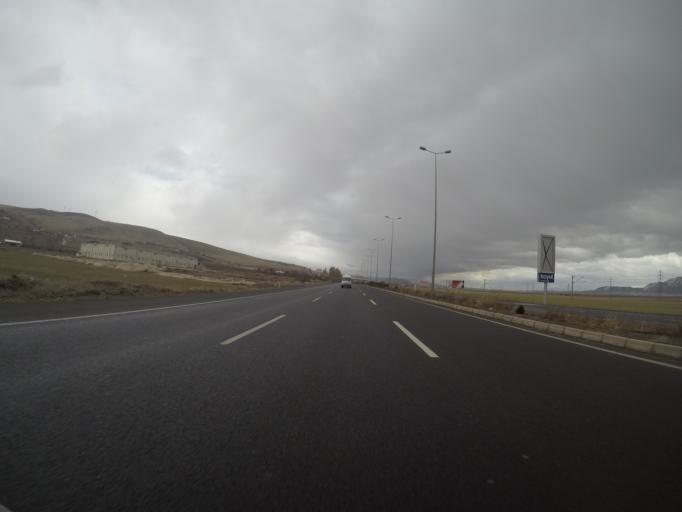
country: TR
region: Kayseri
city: Incesu
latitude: 38.7214
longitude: 35.2735
